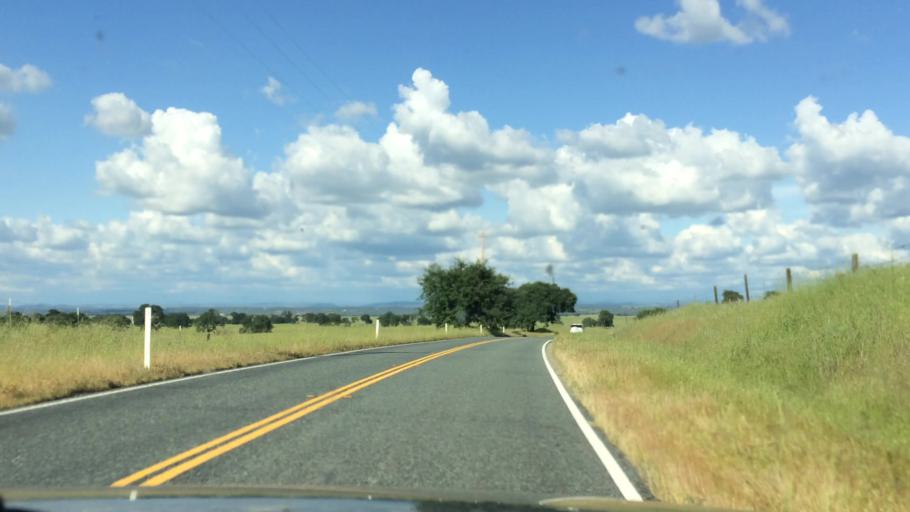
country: US
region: California
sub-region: Sacramento County
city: Clay
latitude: 38.3845
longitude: -121.0522
